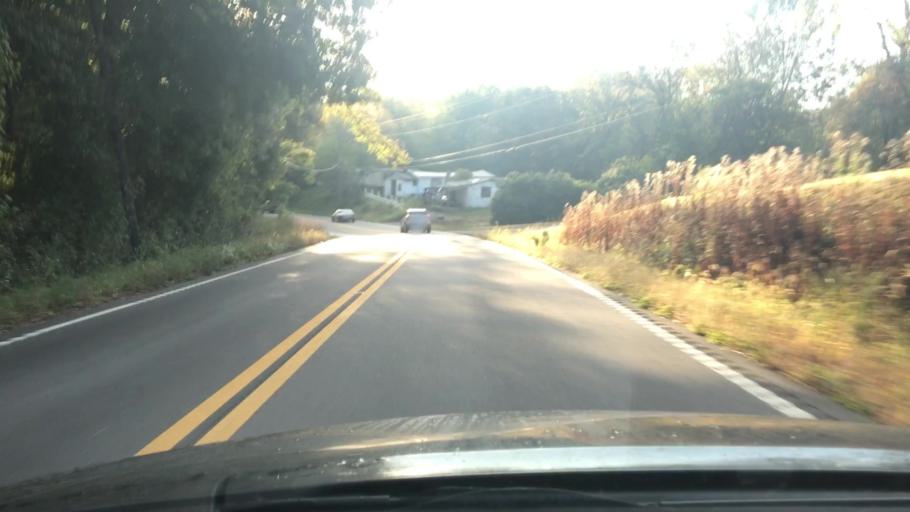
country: US
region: Tennessee
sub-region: Cheatham County
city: Ashland City
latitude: 36.2882
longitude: -87.1629
